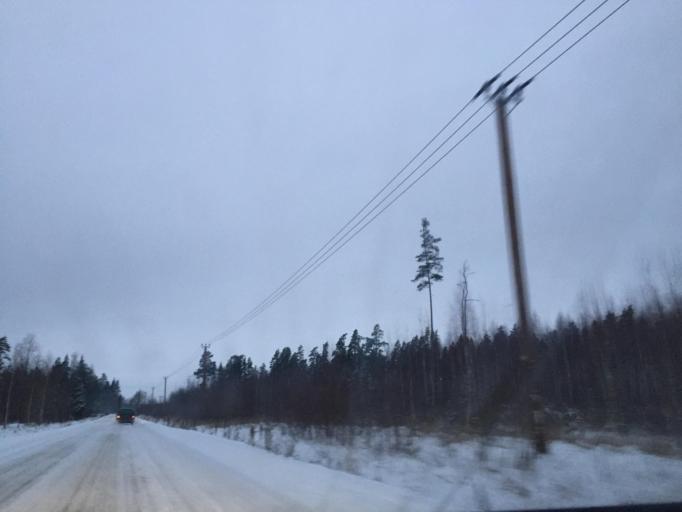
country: LV
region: Raunas
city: Rauna
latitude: 57.4283
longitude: 25.6703
